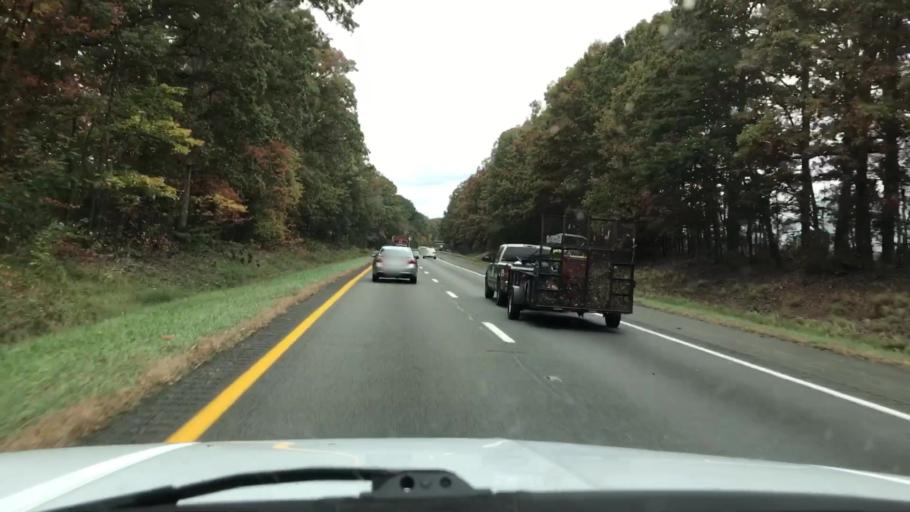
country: US
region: Virginia
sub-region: Goochland County
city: Goochland
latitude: 37.7011
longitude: -77.7503
